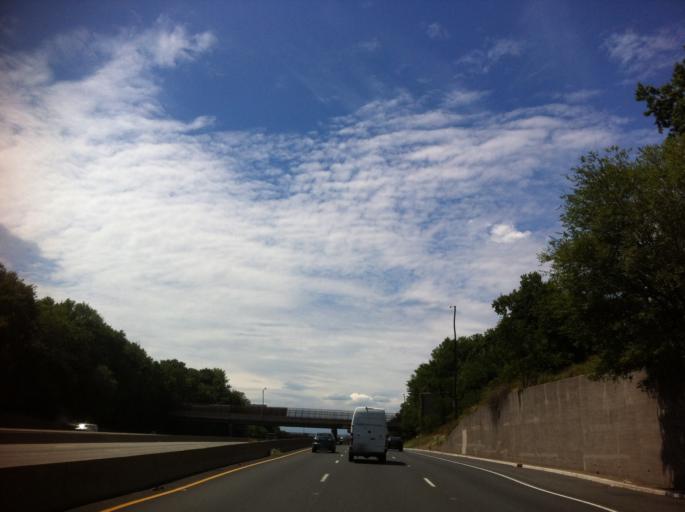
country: US
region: New Jersey
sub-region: Bergen County
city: Ridgefield Park
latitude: 40.8655
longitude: -74.0161
